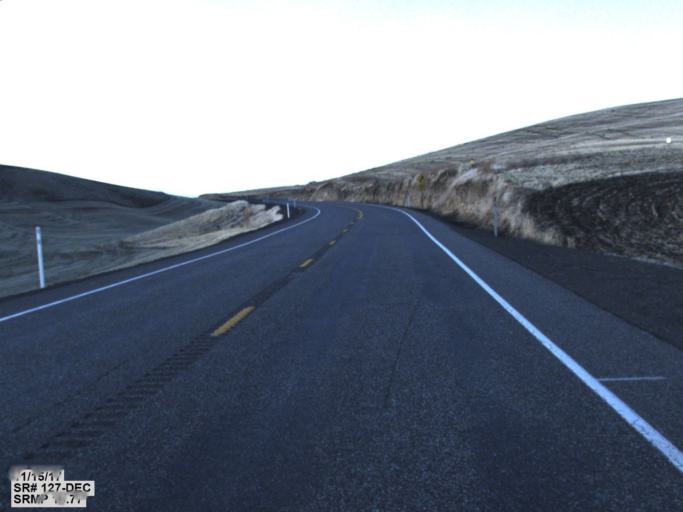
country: US
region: Washington
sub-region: Garfield County
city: Pomeroy
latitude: 46.7275
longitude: -117.7624
